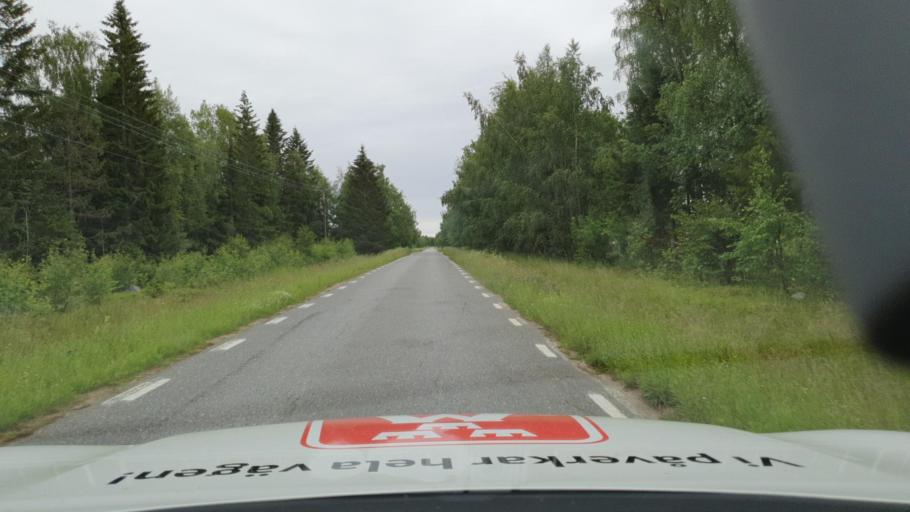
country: SE
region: Vaesterbotten
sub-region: Nordmalings Kommun
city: Nordmaling
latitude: 63.4710
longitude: 19.4628
